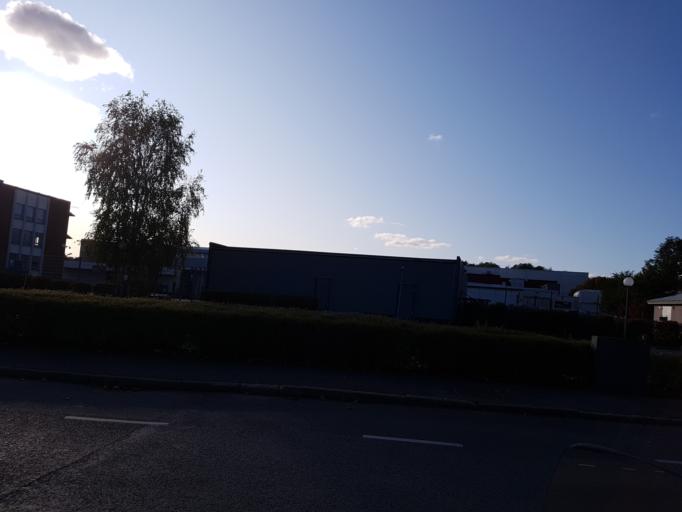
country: SE
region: Vaestra Goetaland
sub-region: Goteborg
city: Hammarkullen
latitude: 57.7504
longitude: 11.9963
